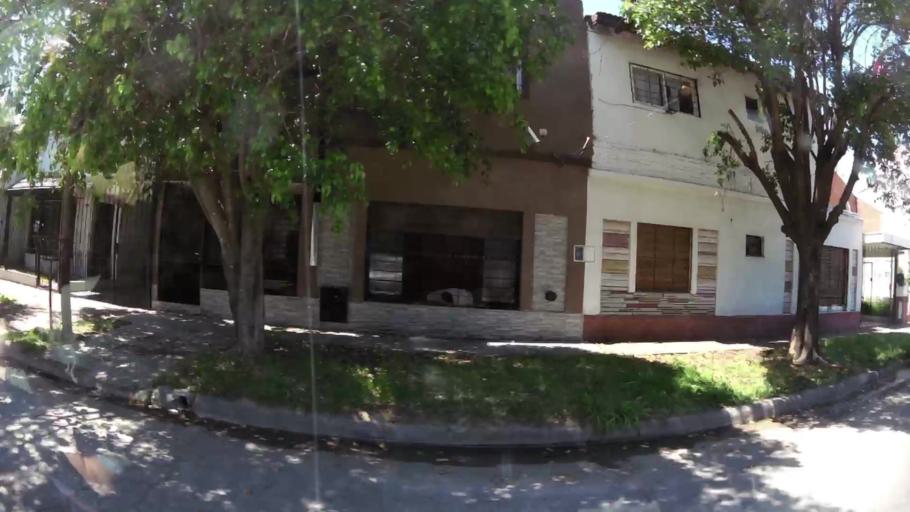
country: AR
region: Buenos Aires
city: Ituzaingo
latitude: -34.6633
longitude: -58.6874
